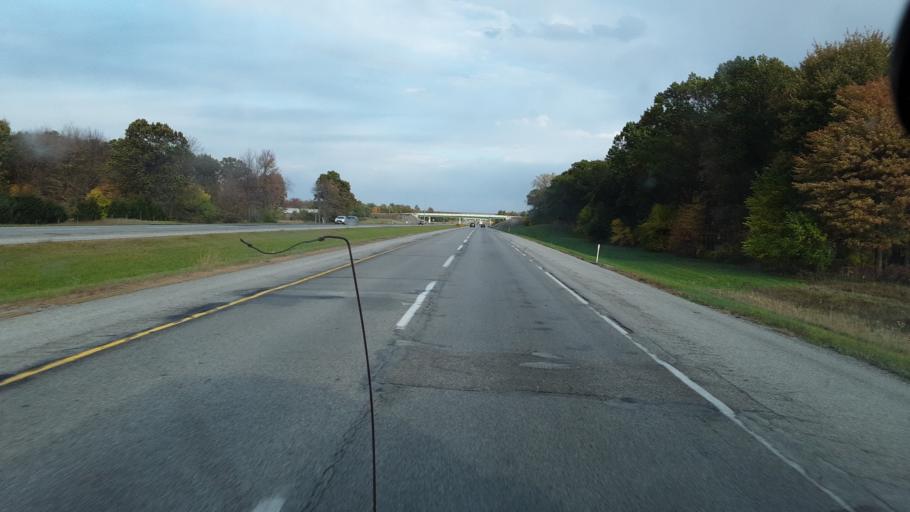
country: US
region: Michigan
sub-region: Saint Joseph County
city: White Pigeon
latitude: 41.7517
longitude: -85.6081
